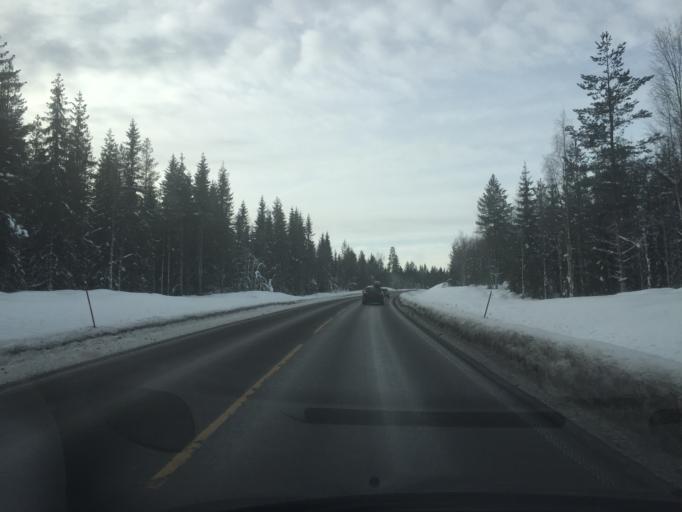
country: NO
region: Hedmark
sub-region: Trysil
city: Innbygda
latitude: 61.2486
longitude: 12.2956
